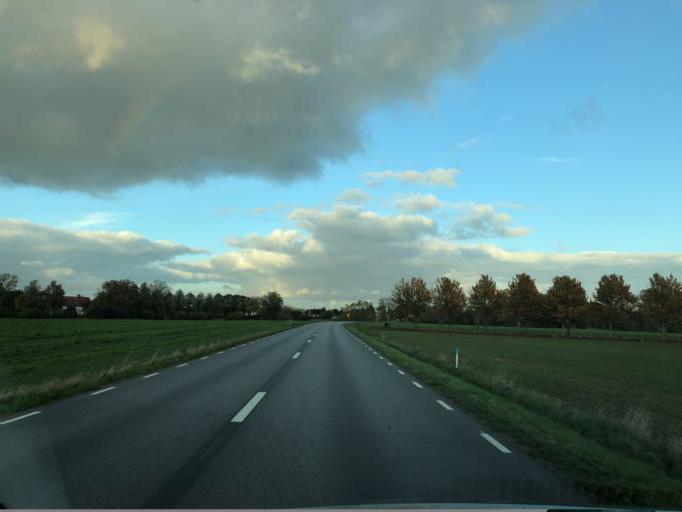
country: SE
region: Skane
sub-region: Svalovs Kommun
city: Teckomatorp
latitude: 55.8602
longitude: 13.1378
